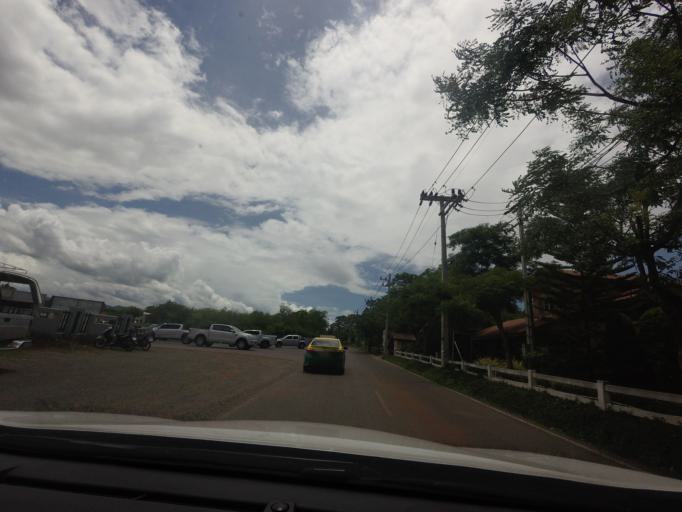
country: TH
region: Nakhon Ratchasima
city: Pak Chong
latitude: 14.5792
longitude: 101.4293
